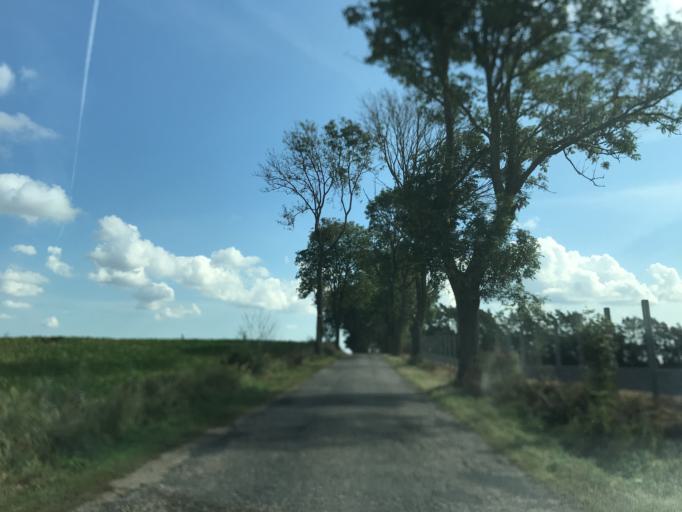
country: PL
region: Kujawsko-Pomorskie
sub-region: Powiat brodnicki
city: Brzozie
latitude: 53.3563
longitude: 19.6250
